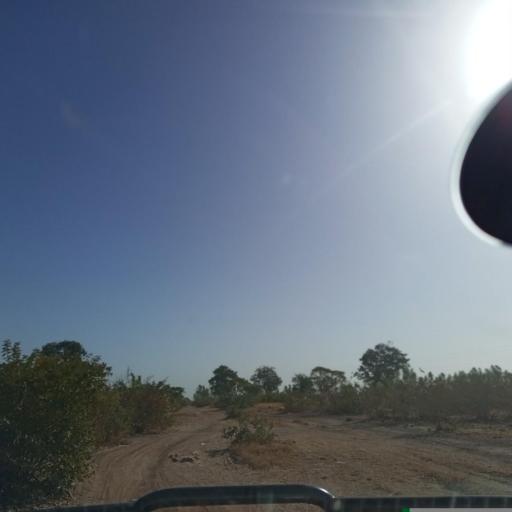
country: ML
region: Koulikoro
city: Koulikoro
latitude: 12.7121
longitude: -7.4176
